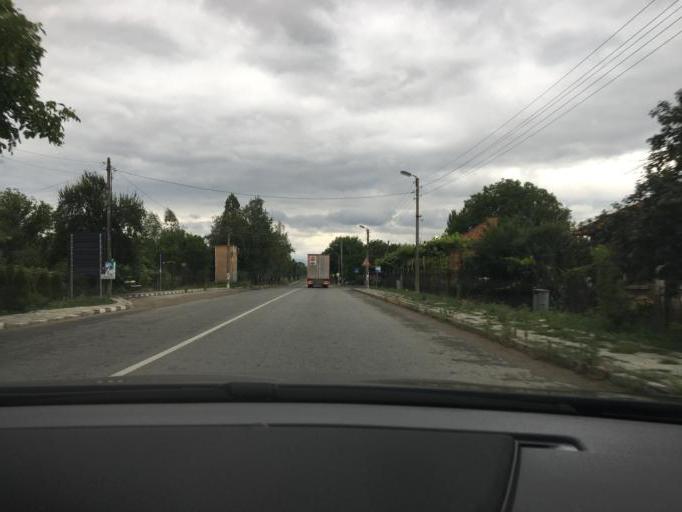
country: BG
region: Kyustendil
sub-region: Obshtina Kyustendil
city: Kyustendil
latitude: 42.2670
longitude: 22.8070
